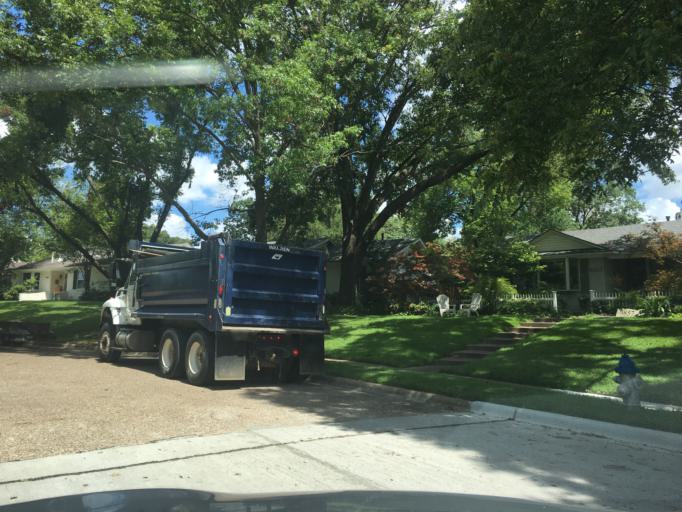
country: US
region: Texas
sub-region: Dallas County
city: Richardson
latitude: 32.8684
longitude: -96.7151
